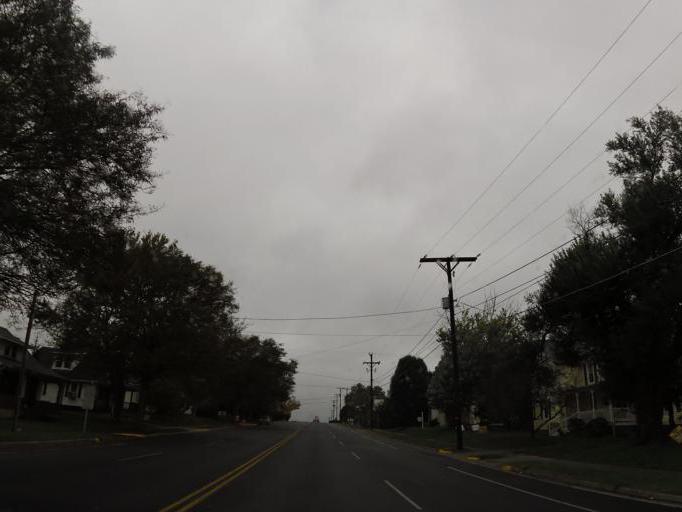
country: US
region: Virginia
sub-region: Wythe County
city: Wytheville
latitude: 36.9446
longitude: -81.0903
